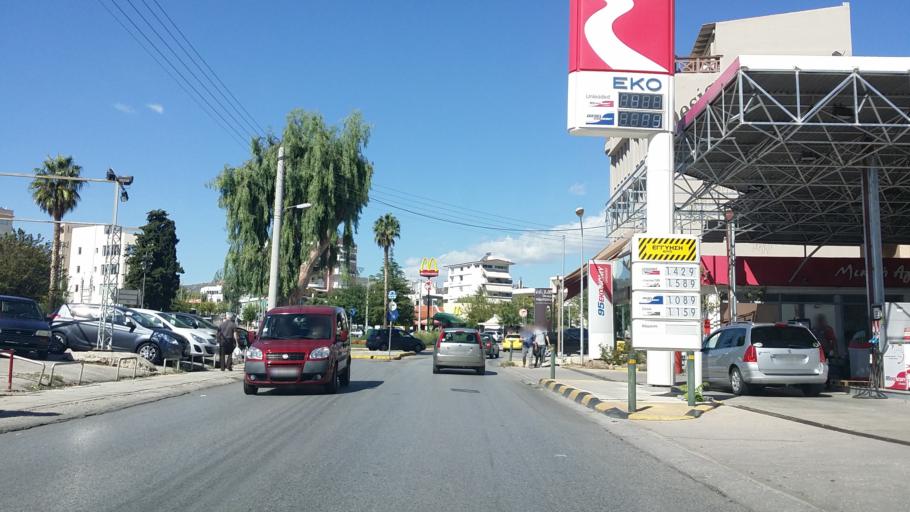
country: GR
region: Attica
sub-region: Nomarchia Athinas
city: Agioi Anargyroi
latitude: 38.0305
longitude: 23.7137
